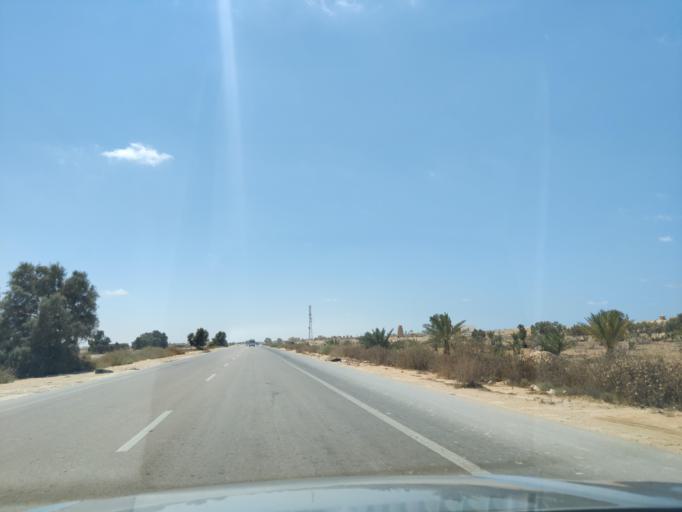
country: EG
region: Muhafazat Matruh
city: Al `Alamayn
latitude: 31.0698
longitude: 28.1426
